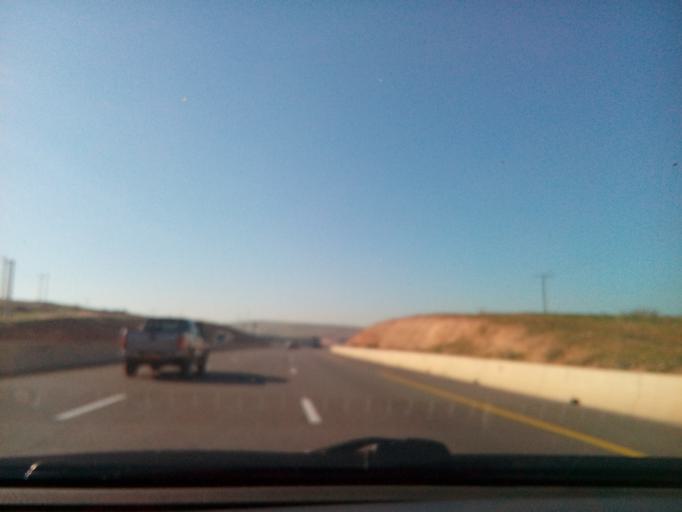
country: DZ
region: Chlef
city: Oued Sly
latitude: 36.0793
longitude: 1.1835
